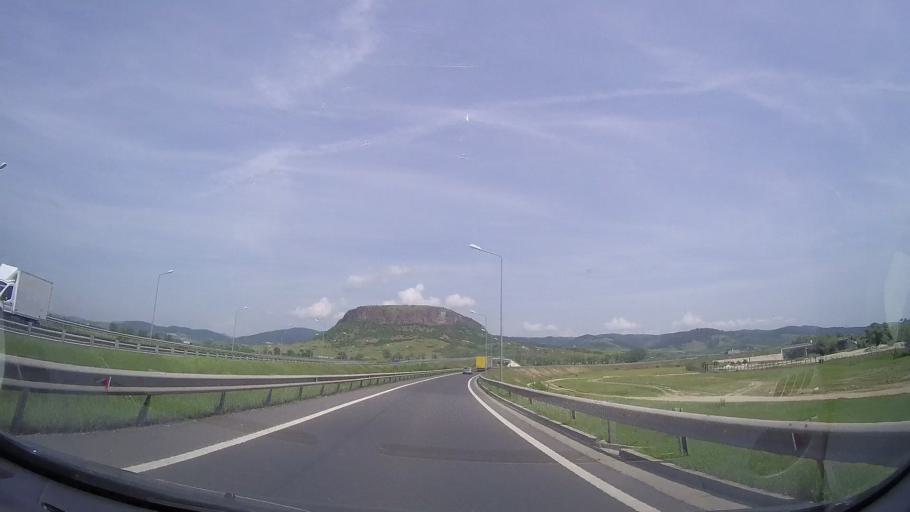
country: RO
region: Hunedoara
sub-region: Oras Simeria
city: Simeria
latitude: 45.8453
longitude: 23.0445
